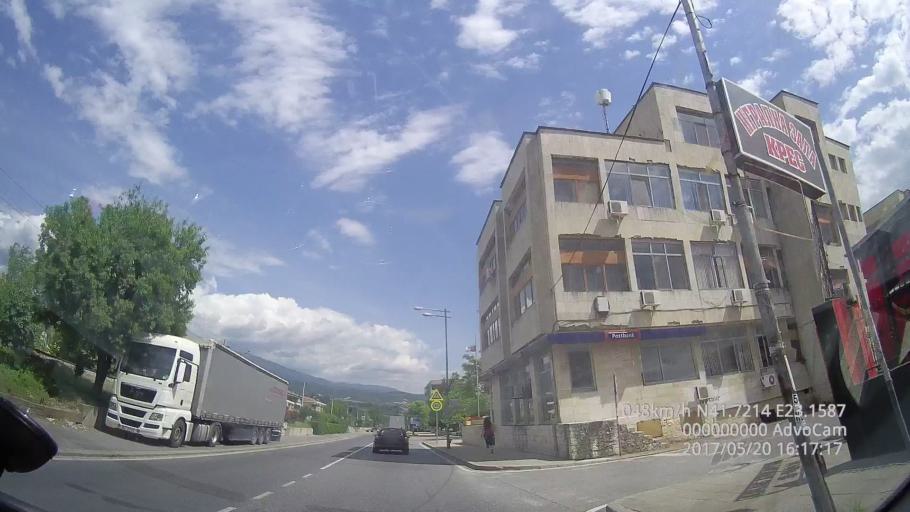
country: BG
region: Blagoevgrad
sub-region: Obshtina Kresna
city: Kresna
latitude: 41.7213
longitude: 23.1590
